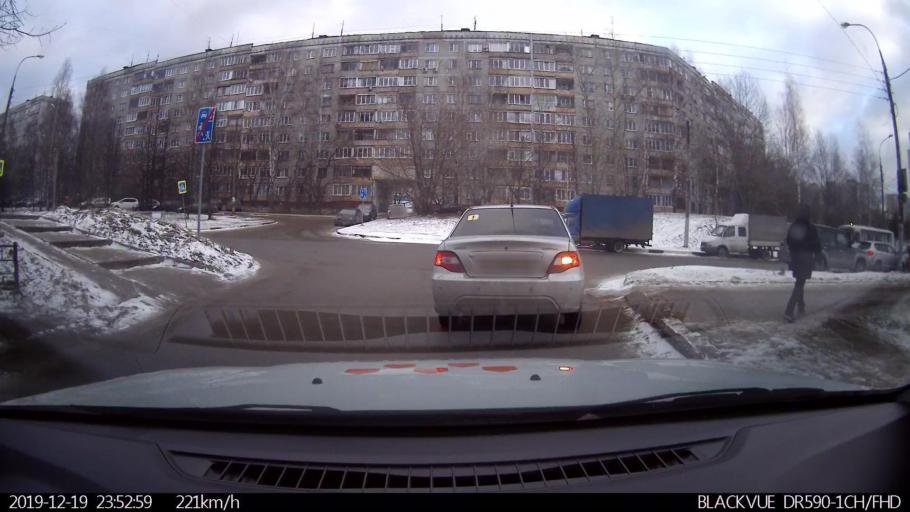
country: RU
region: Vologda
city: Molochnoye
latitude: 58.9722
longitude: 39.4949
